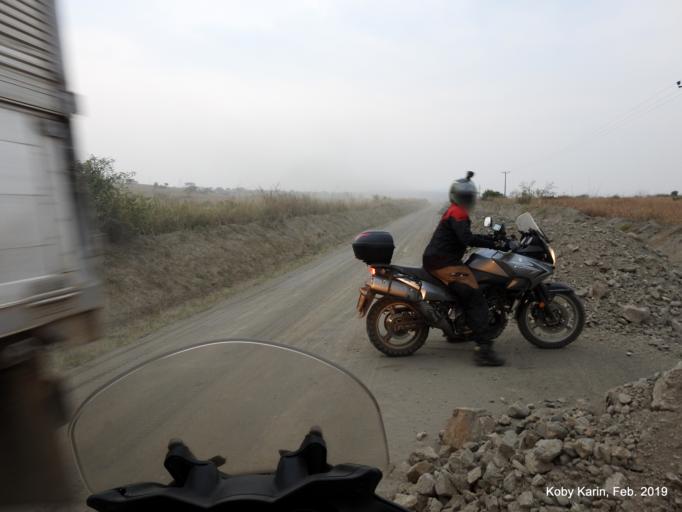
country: UG
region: Western Region
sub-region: Rubirizi District
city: Rubirizi
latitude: -0.1211
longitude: 29.9385
